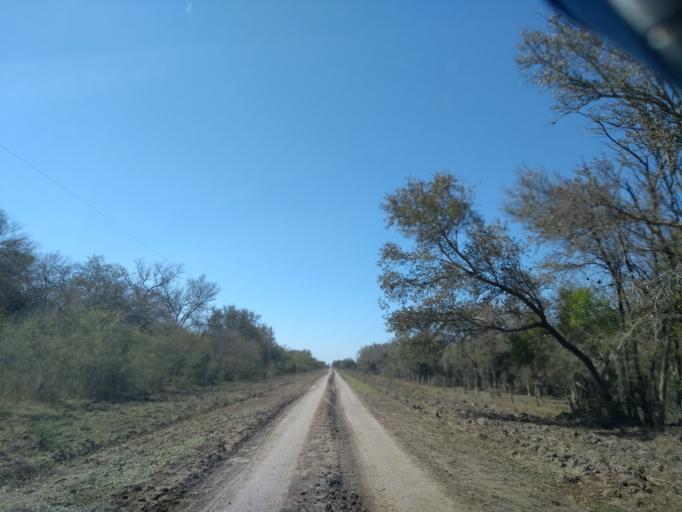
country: AR
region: Chaco
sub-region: Departamento de Quitilipi
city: Quitilipi
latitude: -26.7106
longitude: -60.2097
